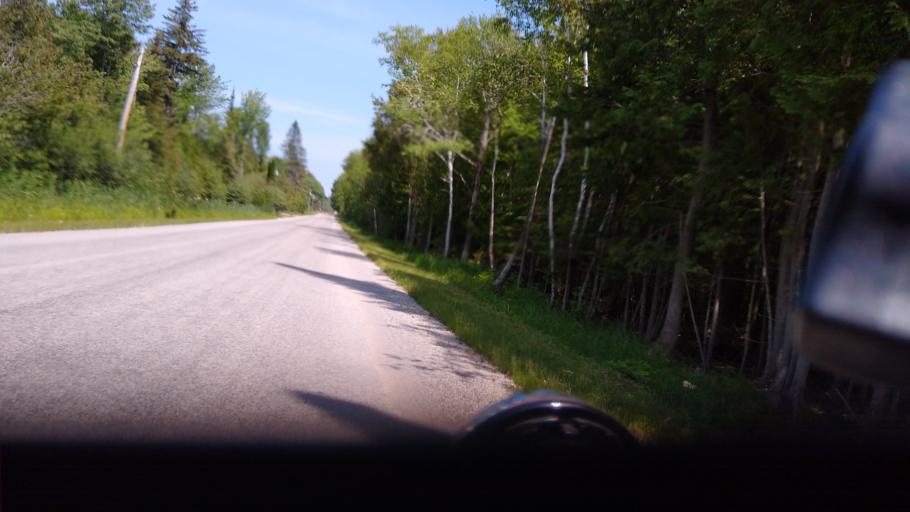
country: US
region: Michigan
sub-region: Delta County
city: Escanaba
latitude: 45.7101
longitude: -87.1479
